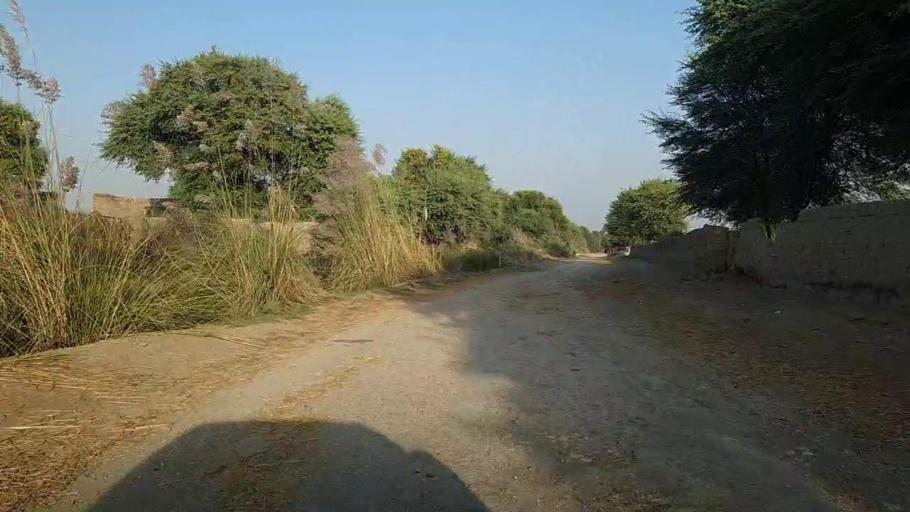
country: PK
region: Sindh
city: Kashmor
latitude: 28.4286
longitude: 69.4586
